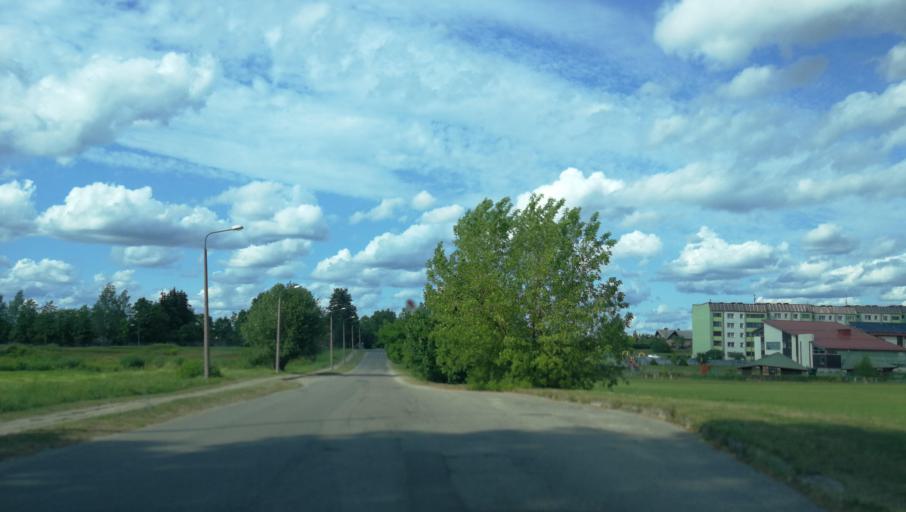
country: LV
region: Cesu Rajons
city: Cesis
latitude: 57.3070
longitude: 25.2890
